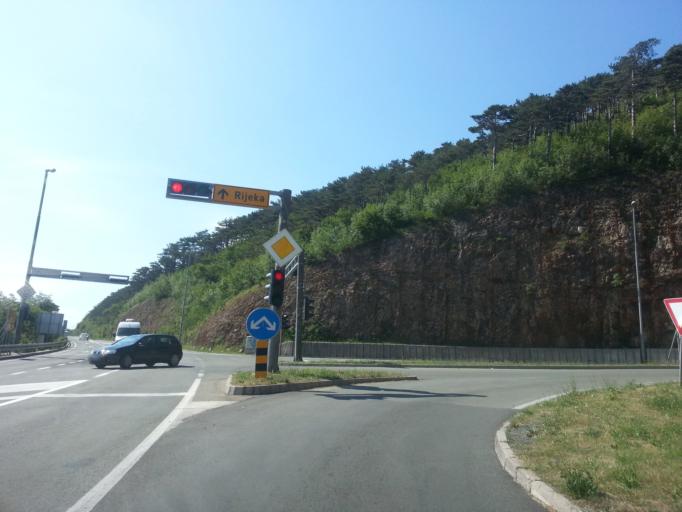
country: HR
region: Primorsko-Goranska
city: Bakar
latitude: 45.3044
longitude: 14.5273
